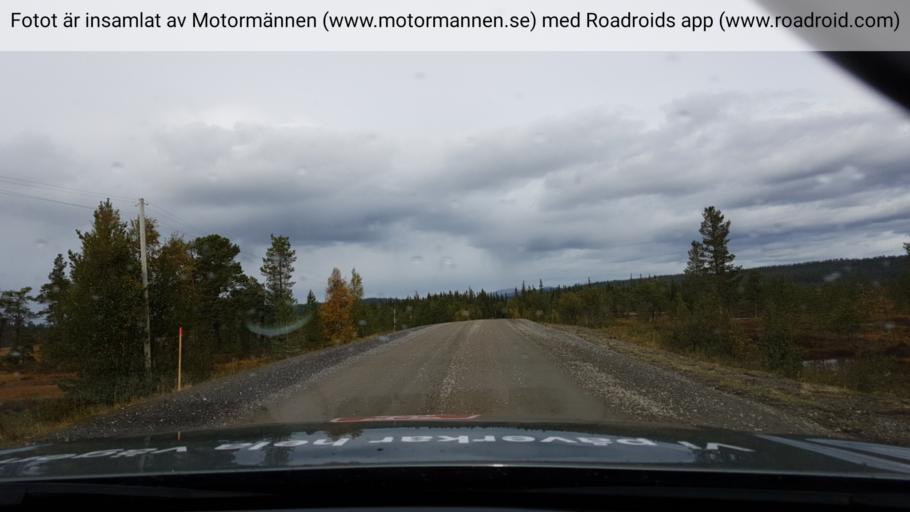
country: NO
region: Nord-Trondelag
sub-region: Snasa
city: Snaase
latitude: 63.7309
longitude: 12.4695
